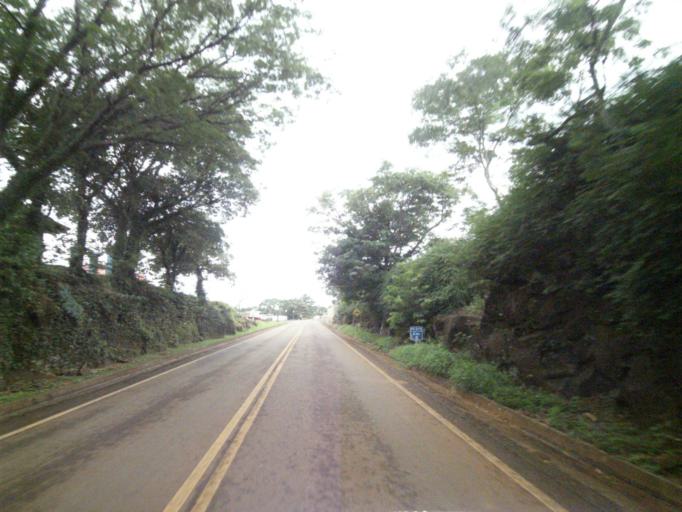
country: BR
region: Parana
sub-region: Guaraniacu
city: Guaraniacu
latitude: -25.0965
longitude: -52.8771
